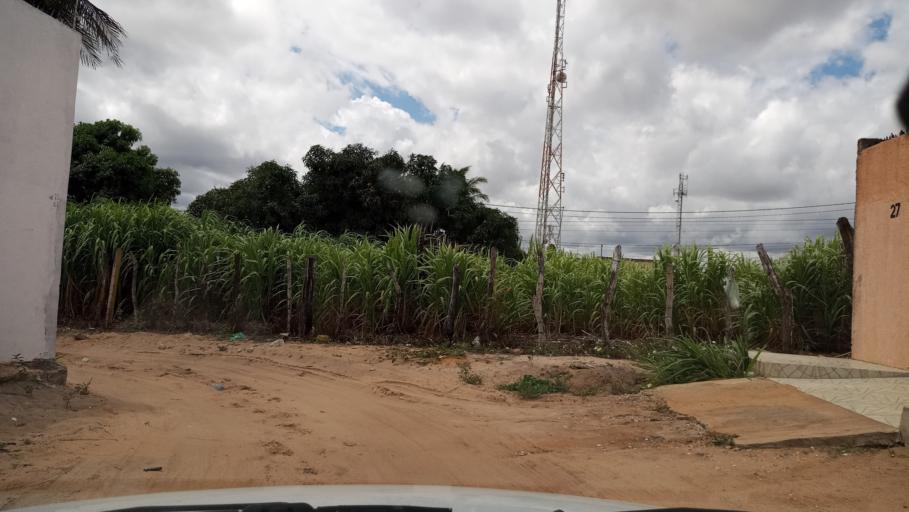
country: BR
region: Rio Grande do Norte
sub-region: Joao Camara
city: Joao Camara
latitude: -5.5361
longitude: -35.8123
